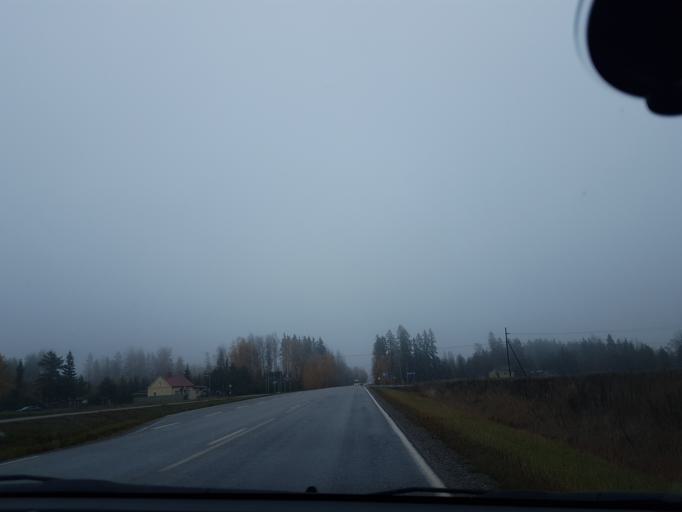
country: FI
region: Uusimaa
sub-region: Helsinki
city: Jaervenpaeae
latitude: 60.4702
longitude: 25.1501
